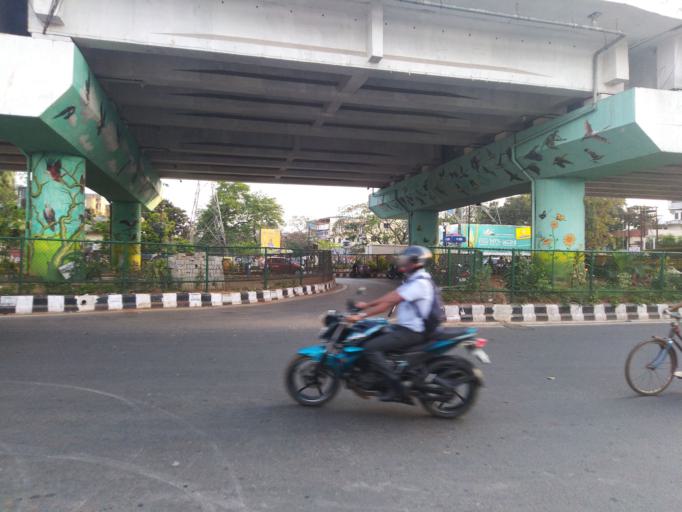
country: IN
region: Odisha
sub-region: Khordha
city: Bhubaneshwar
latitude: 20.2972
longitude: 85.8336
